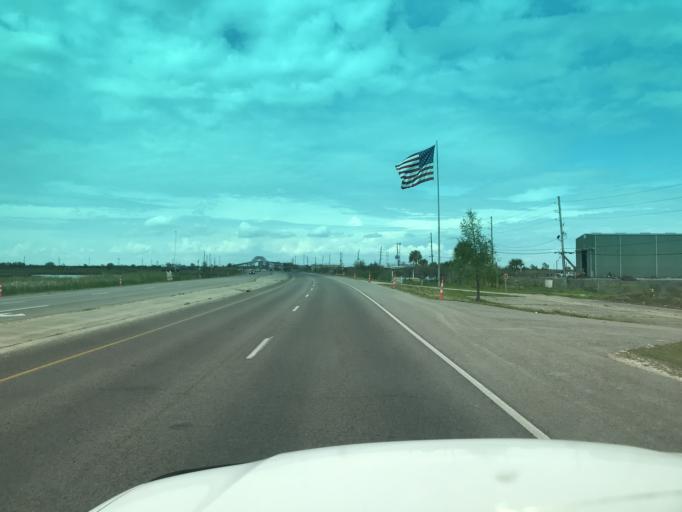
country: US
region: Louisiana
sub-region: Saint Bernard Parish
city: Chalmette
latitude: 29.9767
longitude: -89.9469
